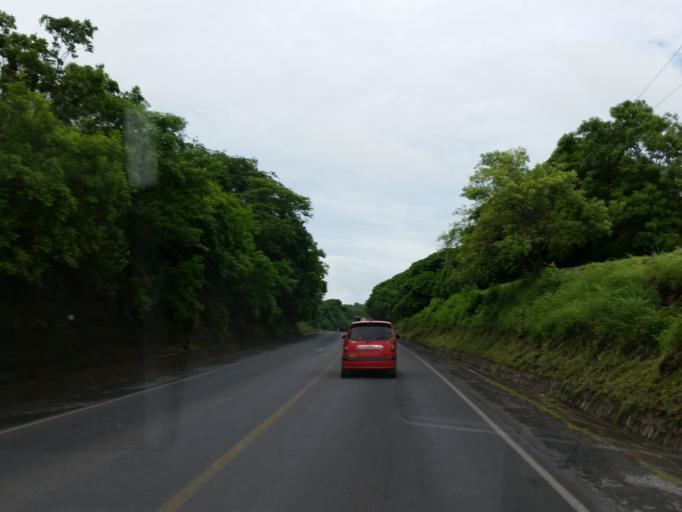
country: NI
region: Leon
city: Nagarote
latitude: 12.2704
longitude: -86.4835
